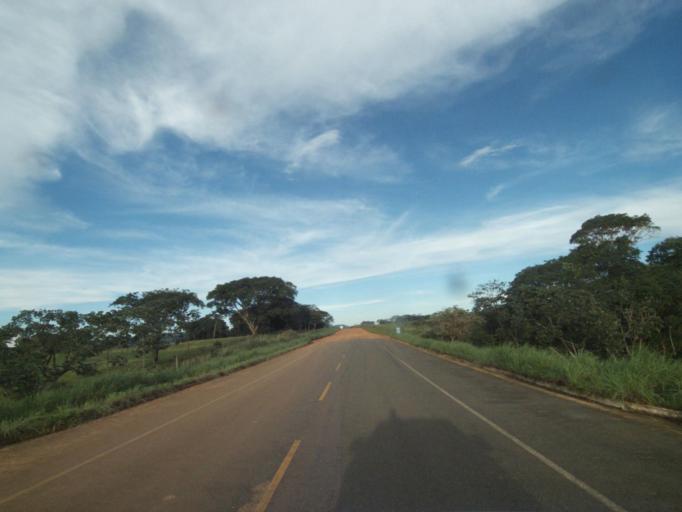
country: BR
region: Goias
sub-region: Jaragua
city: Jaragua
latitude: -15.8376
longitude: -49.2791
